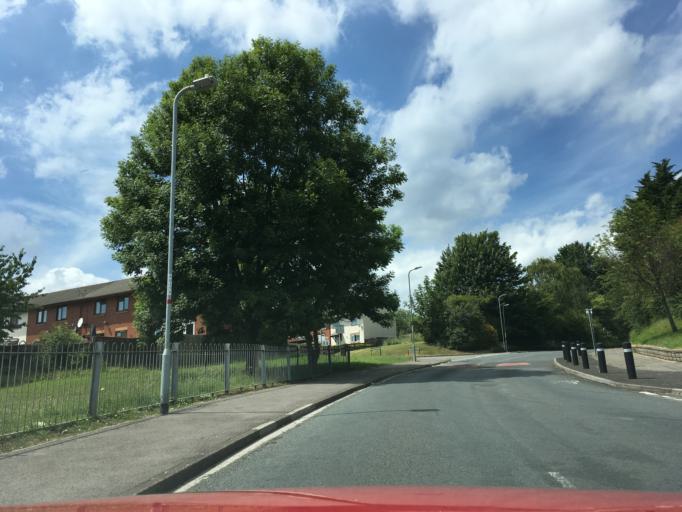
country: GB
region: Wales
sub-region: Newport
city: Caerleon
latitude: 51.5857
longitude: -2.9544
